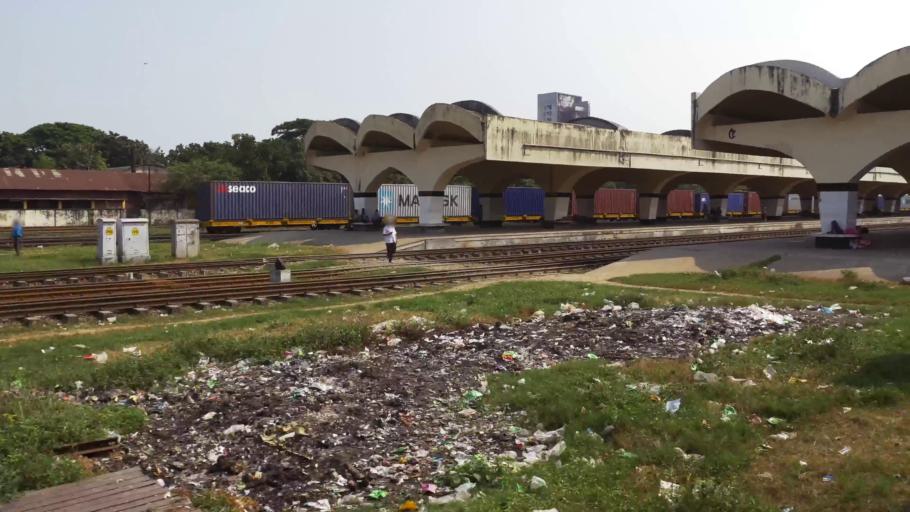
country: BD
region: Dhaka
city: Paltan
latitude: 23.7429
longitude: 90.4263
